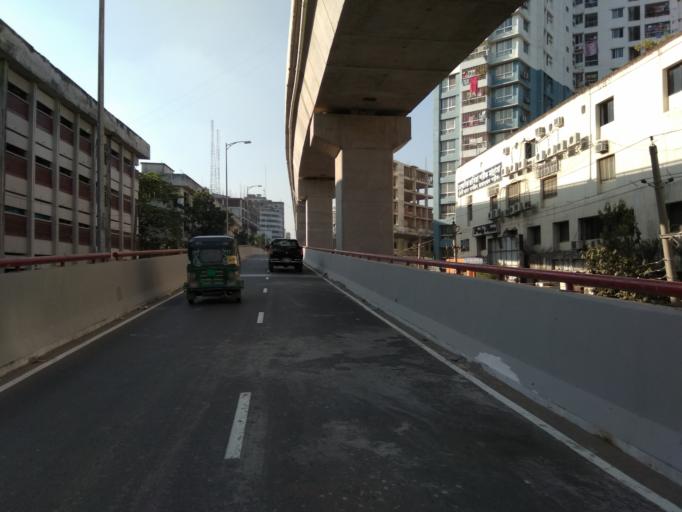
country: BD
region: Dhaka
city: Paltan
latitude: 23.7425
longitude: 90.4165
